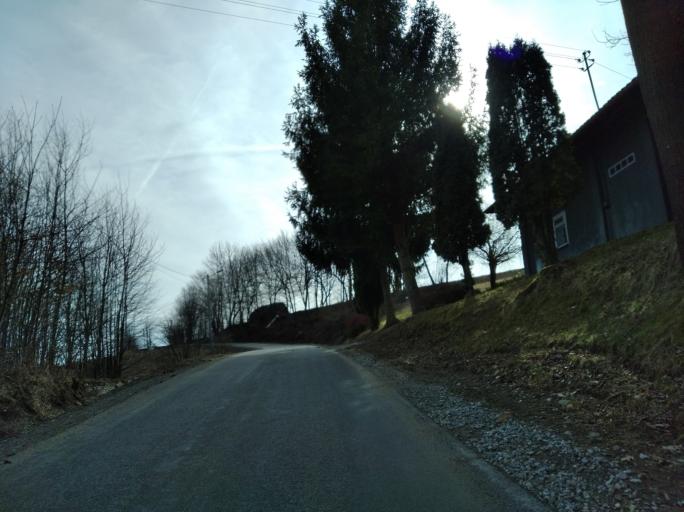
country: PL
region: Subcarpathian Voivodeship
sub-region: Powiat brzozowski
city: Jasienica Rosielna
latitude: 49.7660
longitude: 21.9428
